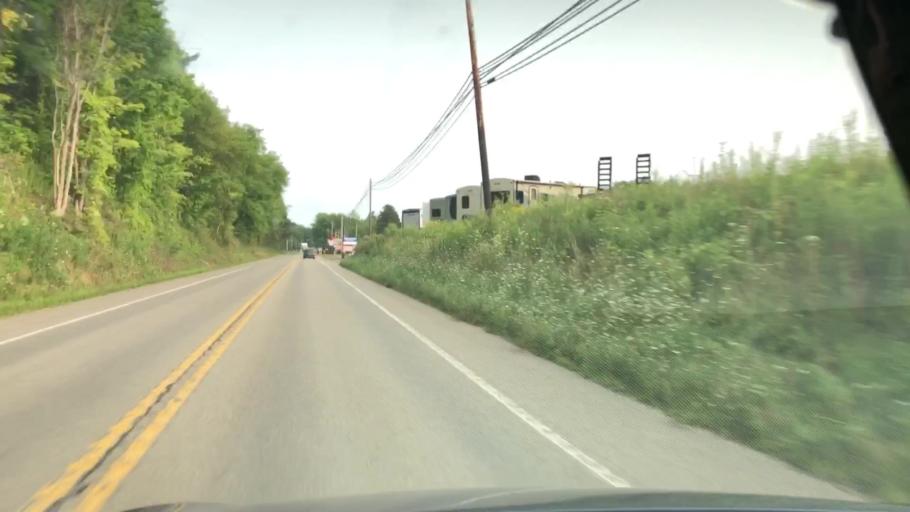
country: US
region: Pennsylvania
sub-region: Crawford County
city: Titusville
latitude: 41.6521
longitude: -79.7222
